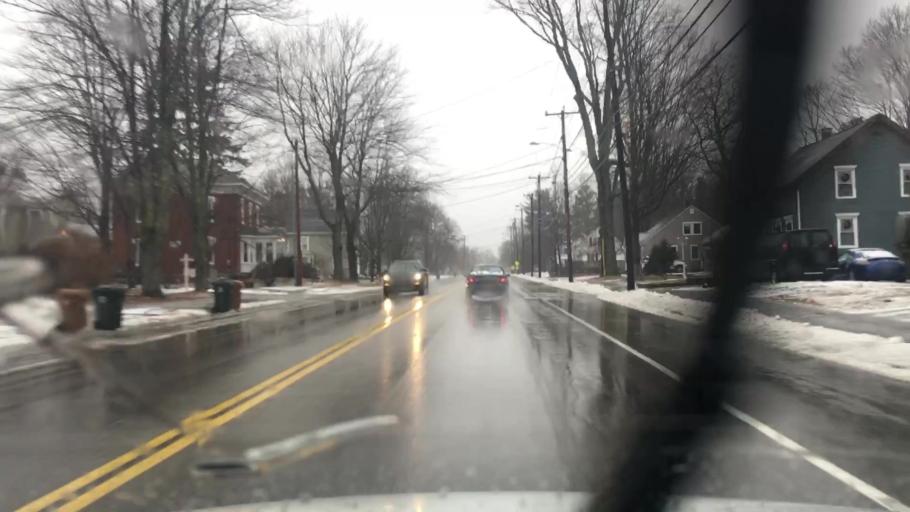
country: US
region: Maine
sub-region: York County
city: Saco
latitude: 43.5096
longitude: -70.4489
